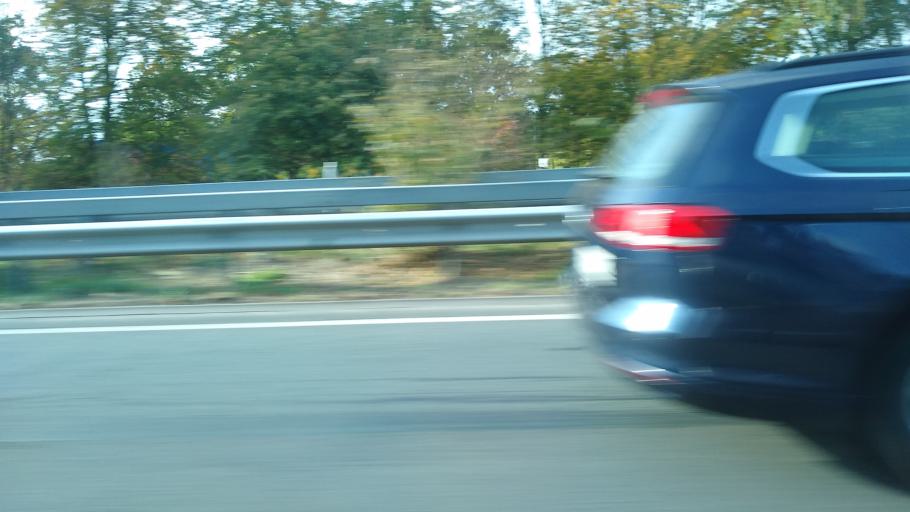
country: DE
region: Lower Saxony
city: Oldenburg
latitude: 53.1781
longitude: 8.2261
